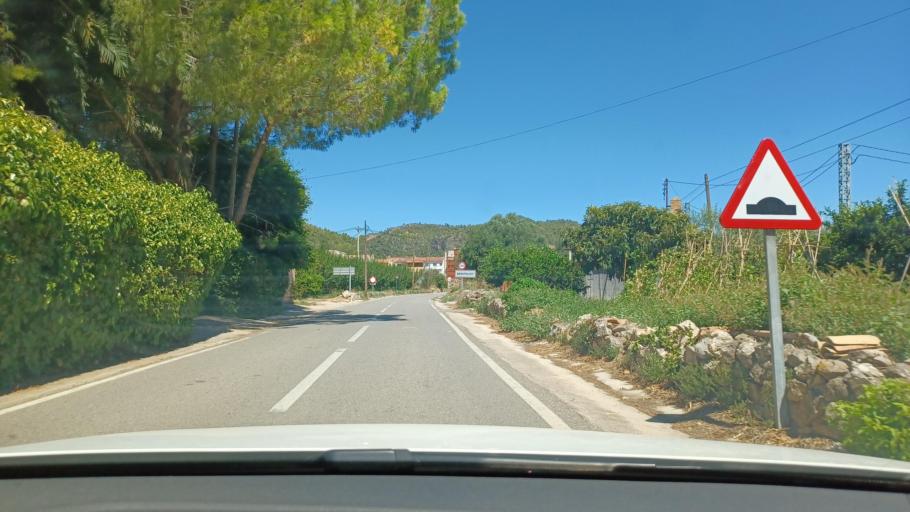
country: ES
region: Catalonia
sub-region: Provincia de Tarragona
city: Benifallet
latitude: 40.9708
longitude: 0.5155
